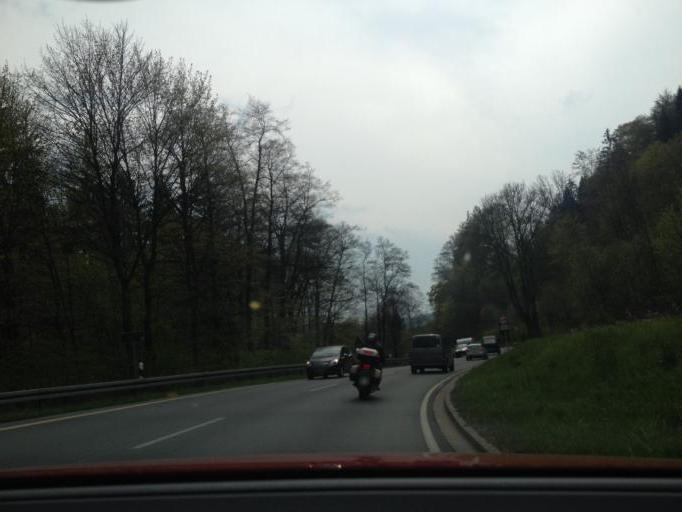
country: DE
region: Bavaria
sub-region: Upper Franconia
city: Goldkronach
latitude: 50.0343
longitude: 11.7106
